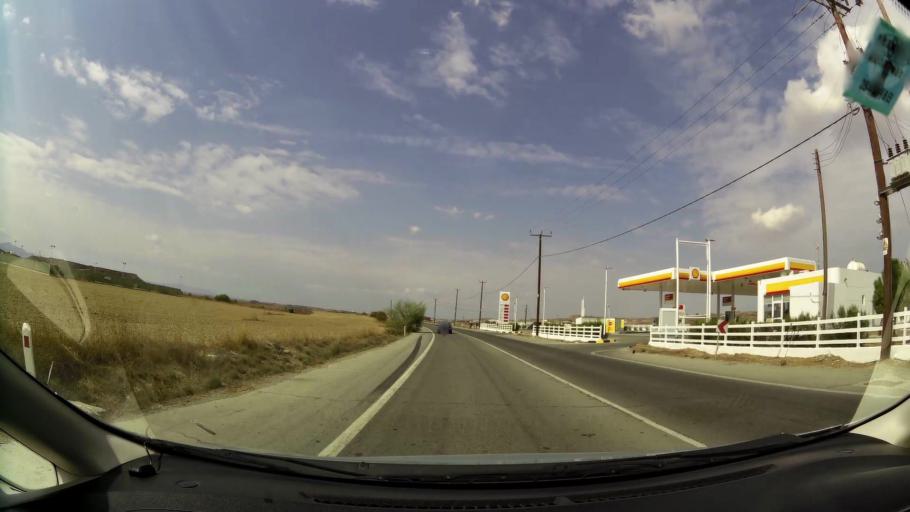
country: CY
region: Lefkosia
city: Tseri
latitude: 35.0587
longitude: 33.3688
